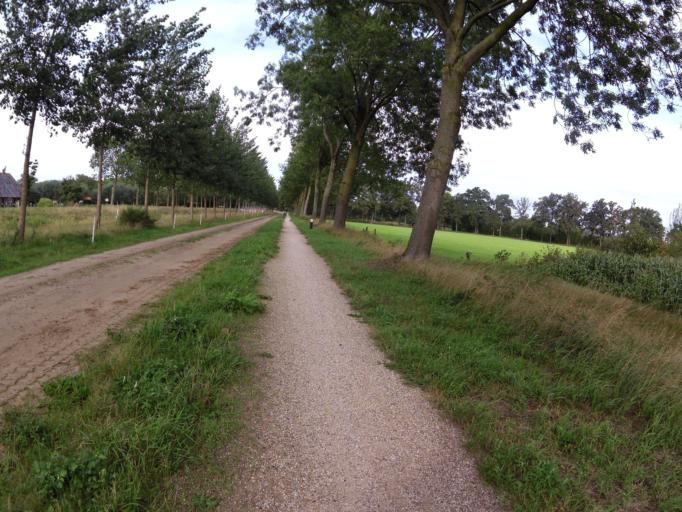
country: NL
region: Gelderland
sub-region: Oude IJsselstreek
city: Varsseveld
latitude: 51.9462
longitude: 6.4887
